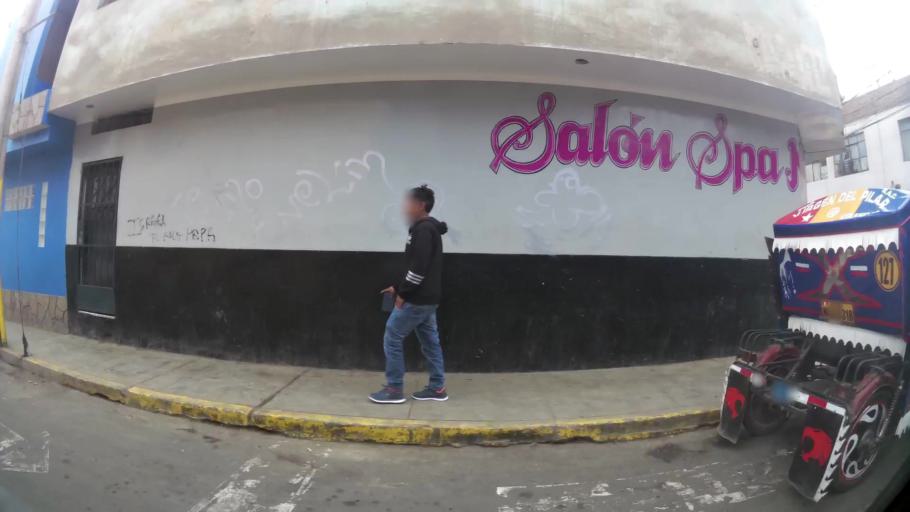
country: PE
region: Lima
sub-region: Provincia de Huaral
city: Huaral
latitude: -11.4965
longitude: -77.2071
